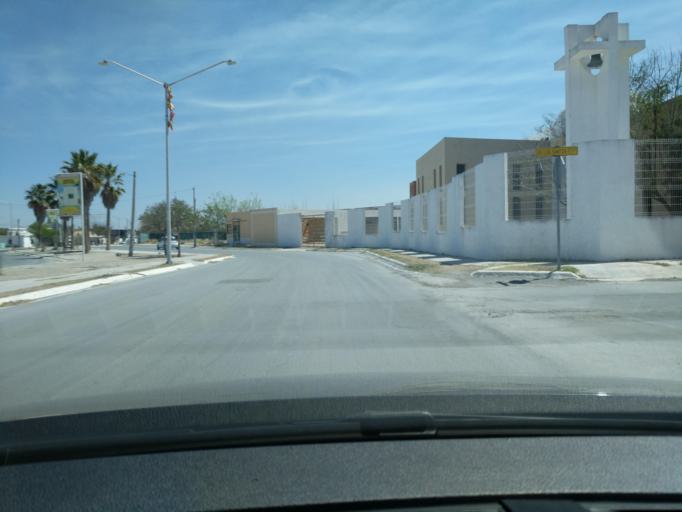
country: MX
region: Nuevo Leon
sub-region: Salinas Victoria
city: Las Torres
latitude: 25.9629
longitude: -100.3047
